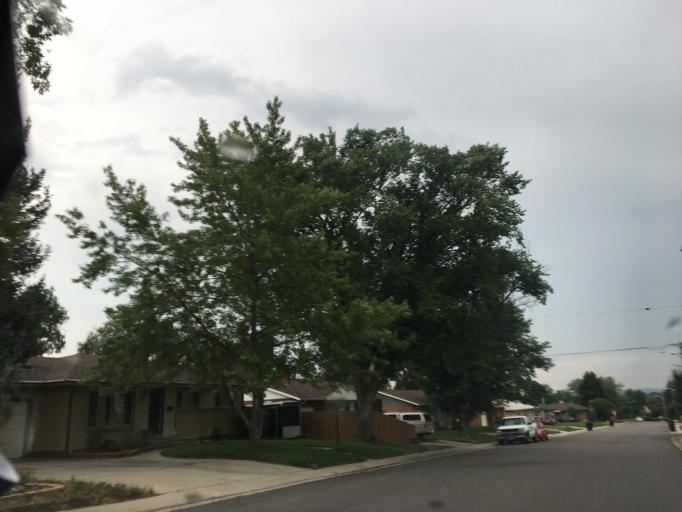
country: US
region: Colorado
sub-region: Arapahoe County
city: Sheridan
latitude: 39.6598
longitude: -105.0395
